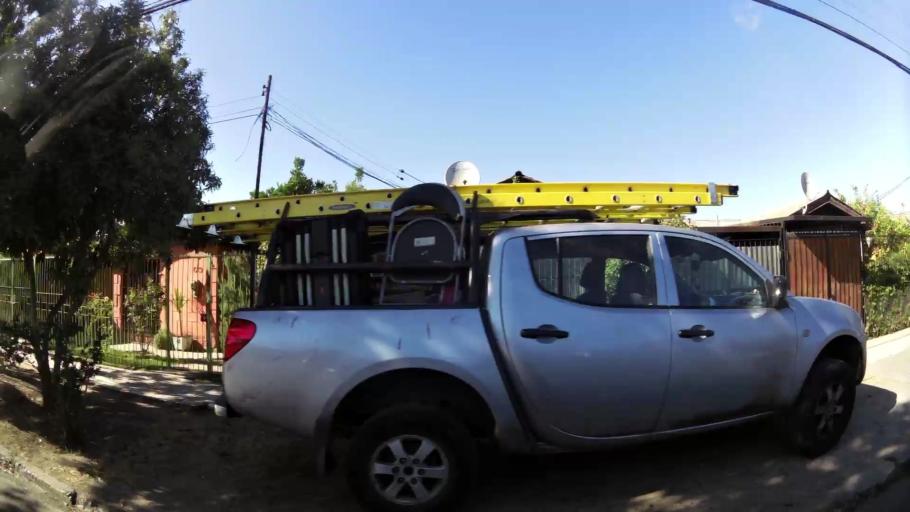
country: CL
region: Santiago Metropolitan
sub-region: Provincia de Maipo
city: San Bernardo
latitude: -33.5516
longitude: -70.6776
